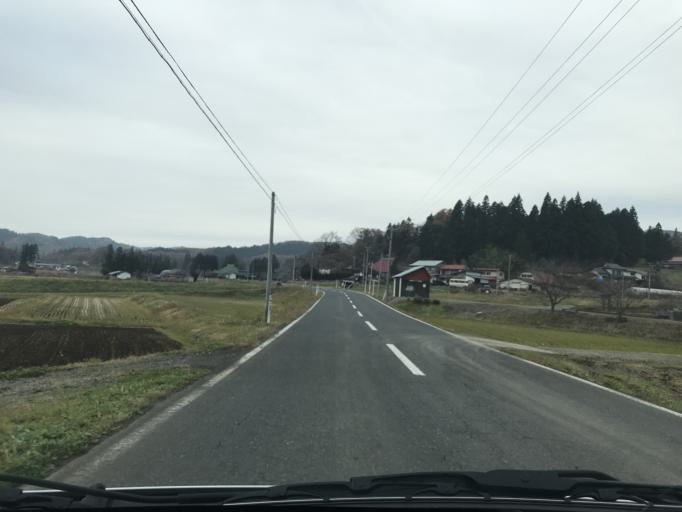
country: JP
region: Iwate
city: Kitakami
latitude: 39.2593
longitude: 141.2006
